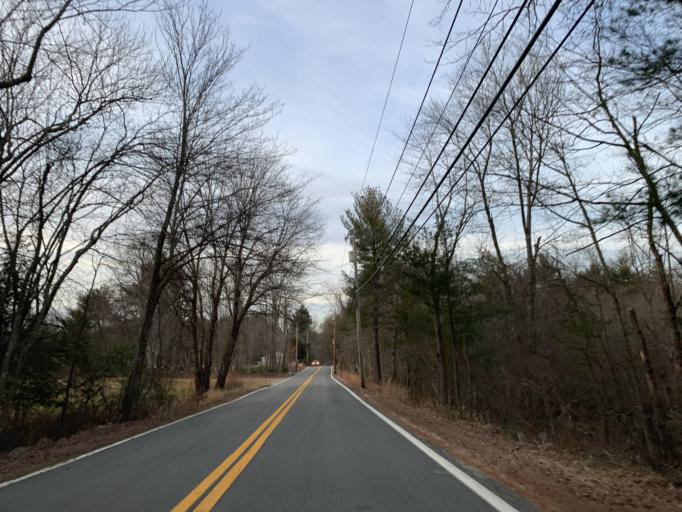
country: US
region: Rhode Island
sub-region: Providence County
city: Pascoag
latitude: 41.9333
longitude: -71.7015
